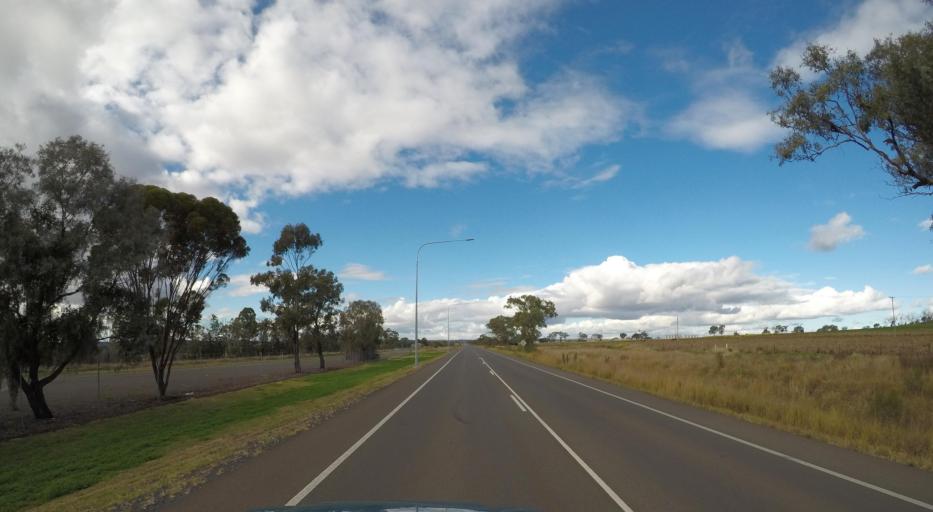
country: AU
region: Queensland
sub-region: Toowoomba
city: Westbrook
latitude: -27.7230
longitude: 151.6029
